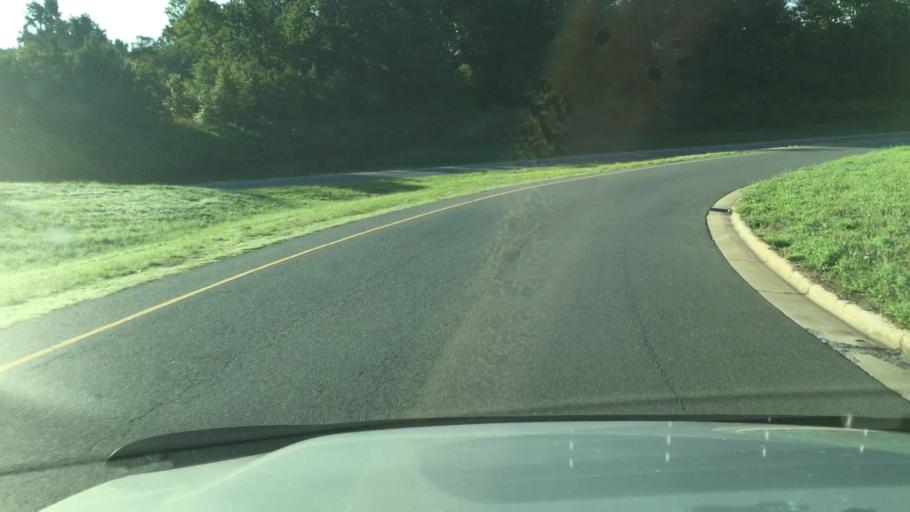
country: US
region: North Carolina
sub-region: Gaston County
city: Mount Holly
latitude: 35.2901
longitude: -80.9623
